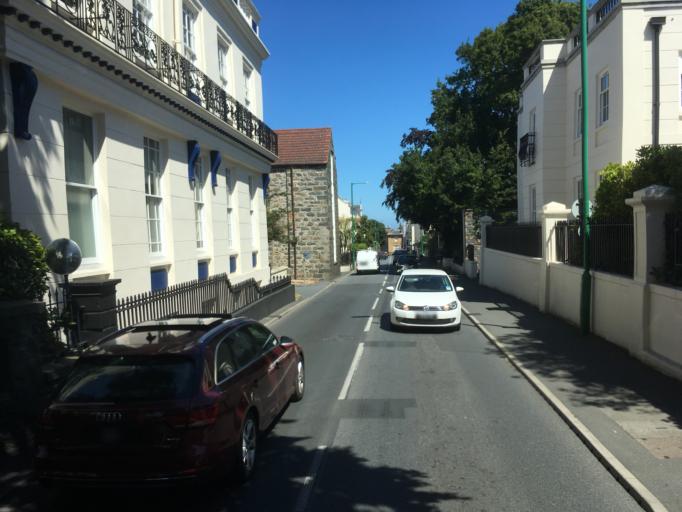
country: GG
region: St Peter Port
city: Saint Peter Port
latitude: 49.4560
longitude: -2.5427
